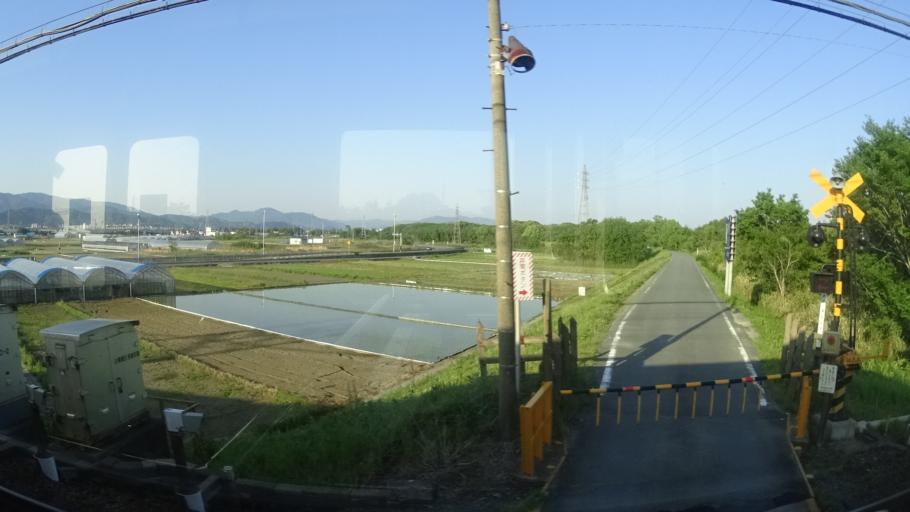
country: JP
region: Mie
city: Ise
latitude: 34.5077
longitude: 136.6916
